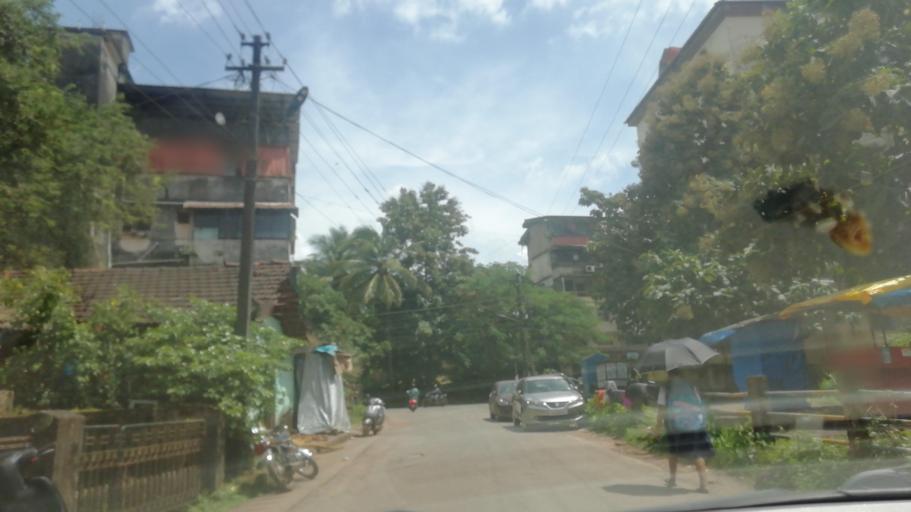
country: IN
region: Goa
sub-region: North Goa
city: Queula
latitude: 15.3942
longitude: 74.0011
